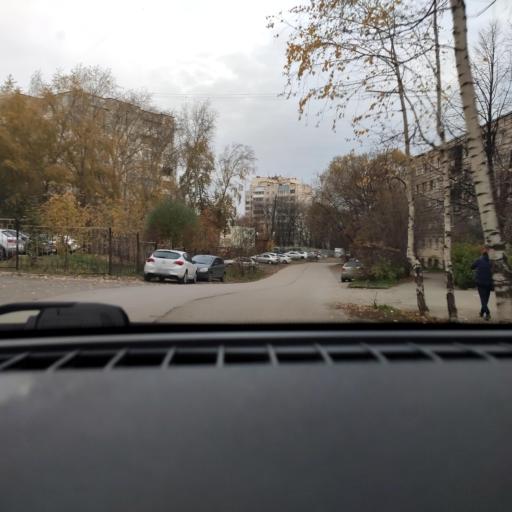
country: RU
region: Perm
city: Perm
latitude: 57.9984
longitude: 56.1963
